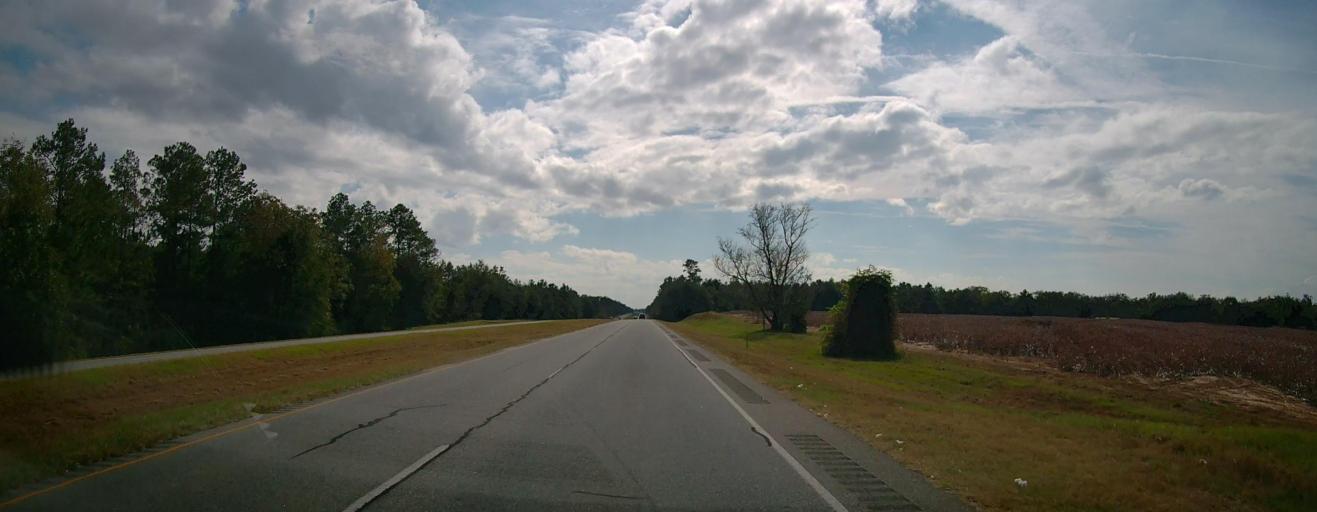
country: US
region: Georgia
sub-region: Mitchell County
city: Camilla
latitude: 31.3141
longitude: -84.1757
